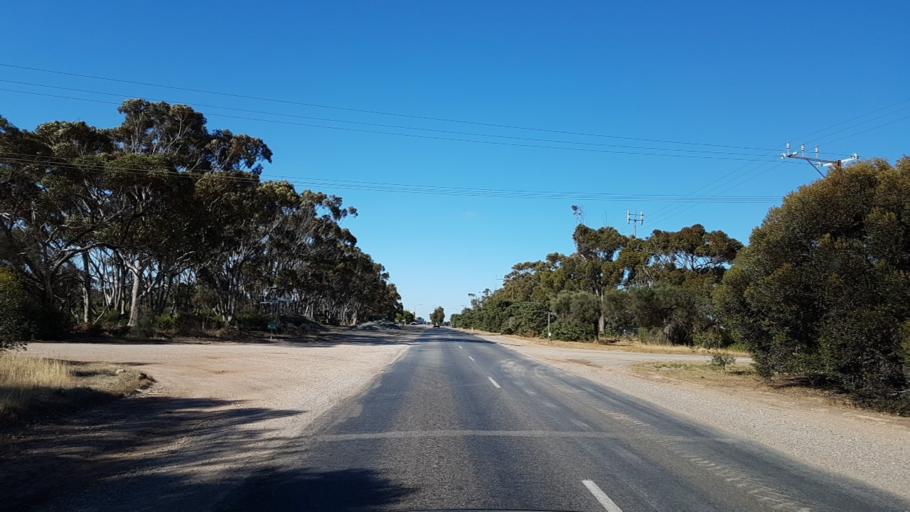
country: AU
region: South Australia
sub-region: Yorke Peninsula
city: Port Victoria
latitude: -34.7779
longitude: 137.5923
